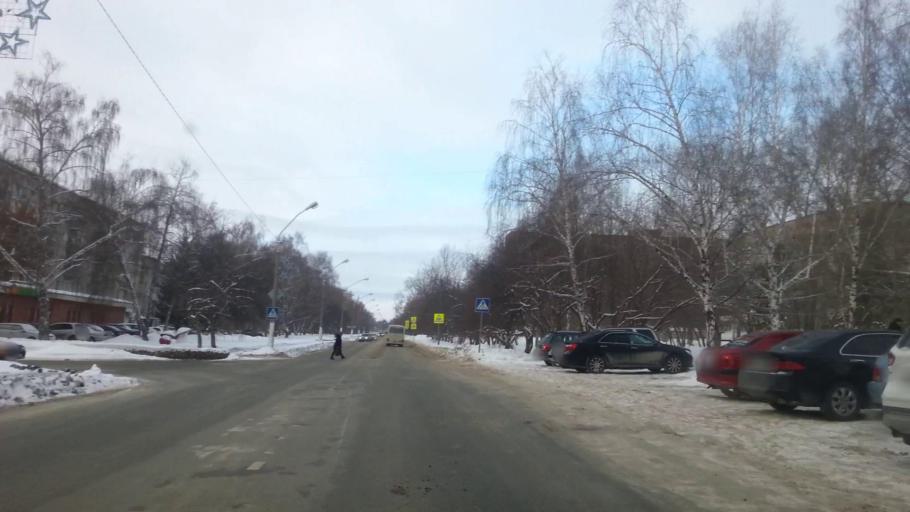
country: RU
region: Altai Krai
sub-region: Gorod Barnaulskiy
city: Barnaul
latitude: 53.3657
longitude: 83.6888
